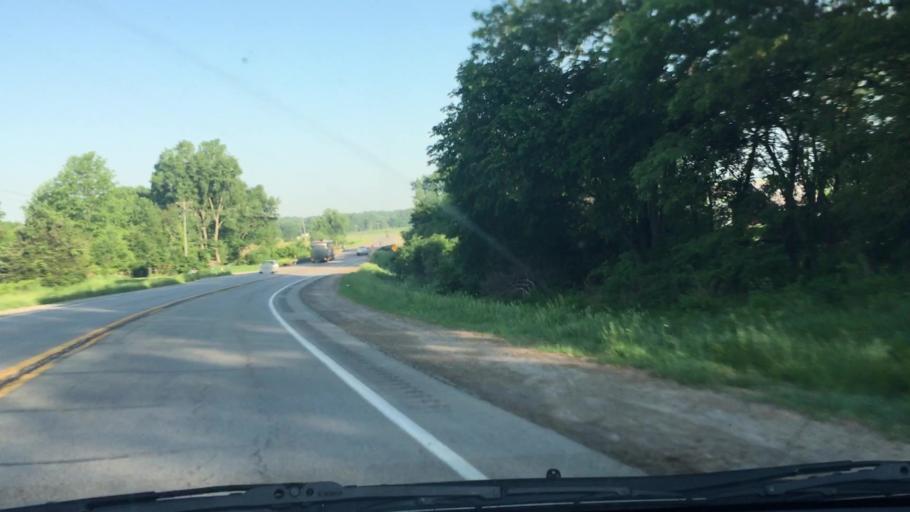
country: US
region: Iowa
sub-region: Johnson County
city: Tiffin
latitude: 41.7118
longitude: -91.6974
